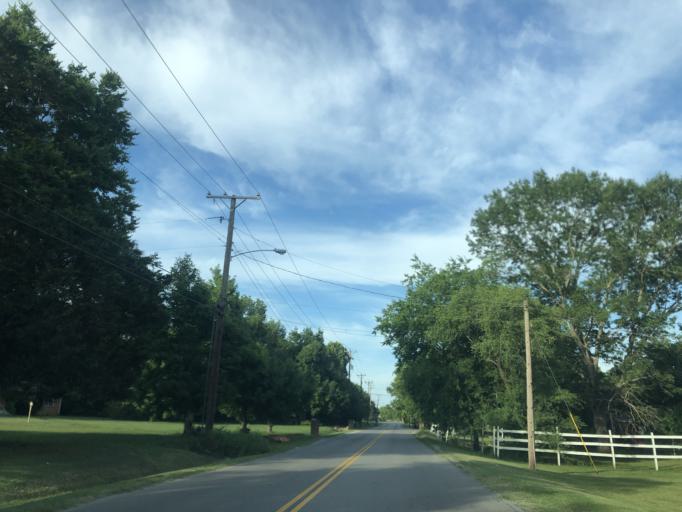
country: US
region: Tennessee
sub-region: Davidson County
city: Nashville
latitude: 36.2105
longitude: -86.8528
